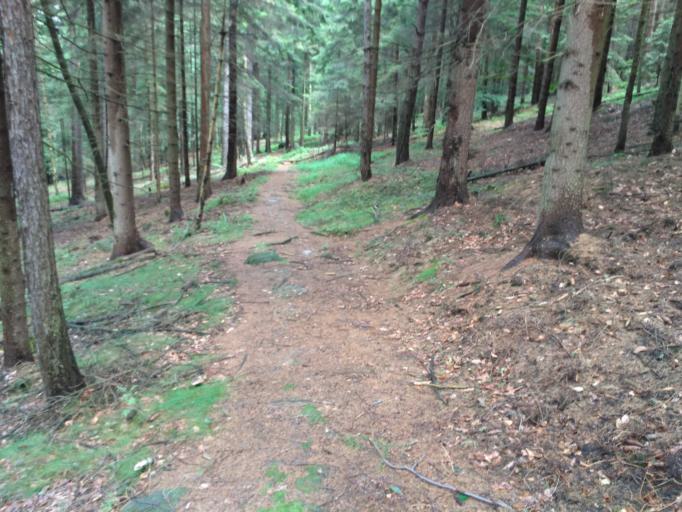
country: DE
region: Saxony
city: Bad Schandau
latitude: 50.8720
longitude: 14.1684
